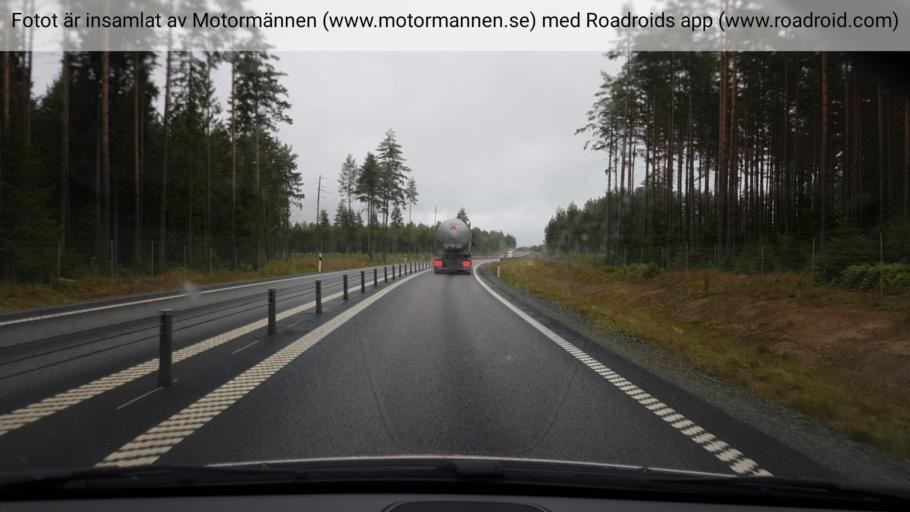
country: SE
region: Uppsala
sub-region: Heby Kommun
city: Heby
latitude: 59.9712
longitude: 16.8364
